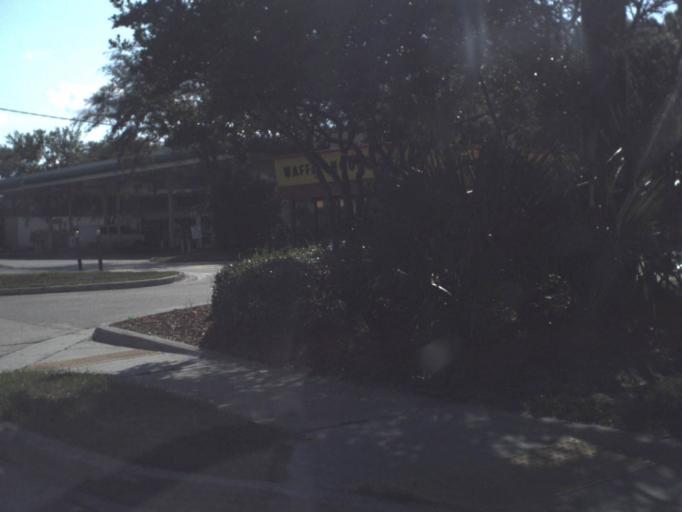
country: US
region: Florida
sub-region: Duval County
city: Jacksonville
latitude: 30.2454
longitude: -81.5985
